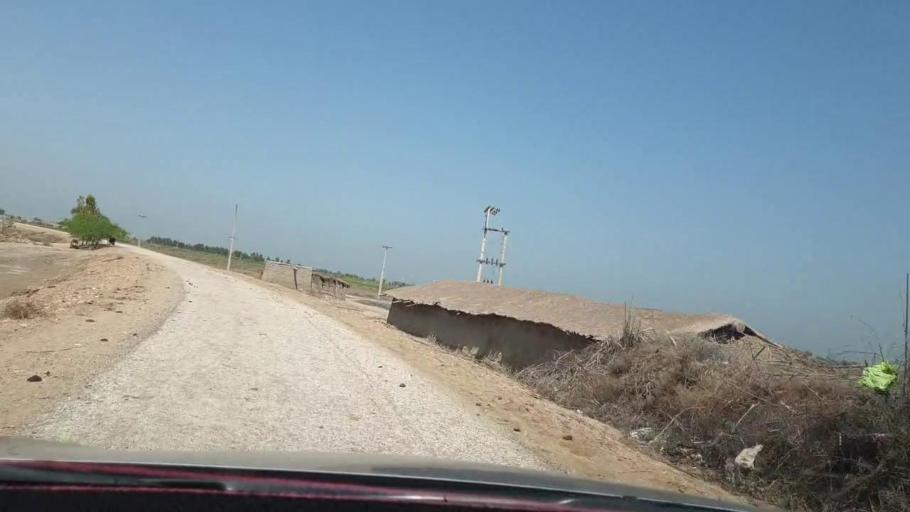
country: PK
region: Sindh
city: Warah
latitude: 27.5411
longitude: 67.7436
